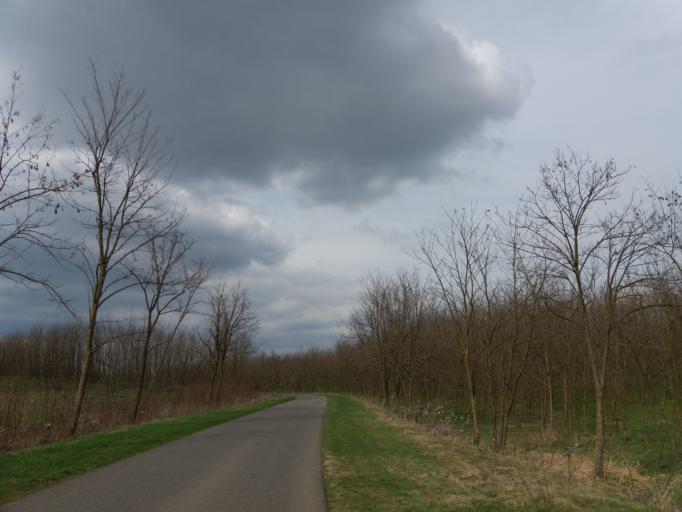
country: HU
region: Szabolcs-Szatmar-Bereg
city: Petnehaza
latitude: 48.0703
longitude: 22.0452
